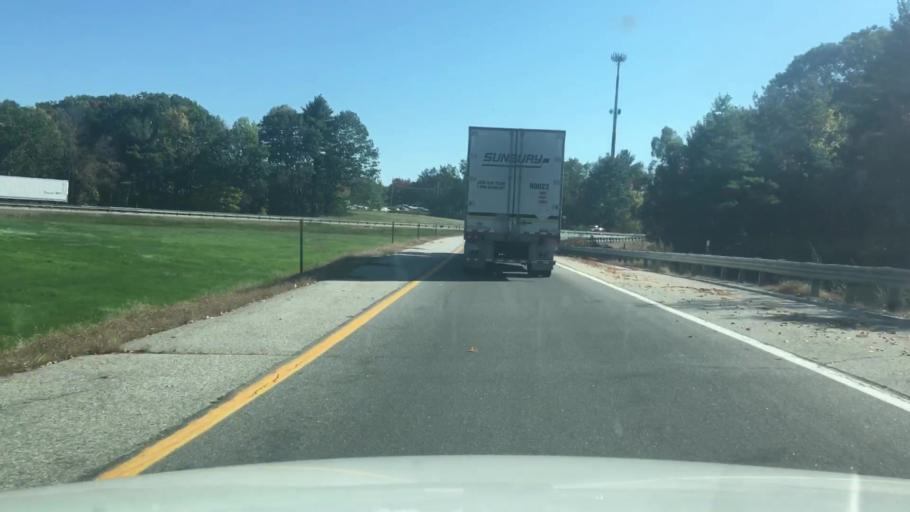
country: US
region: Maine
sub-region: Cumberland County
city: Falmouth
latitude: 43.7193
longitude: -70.3071
